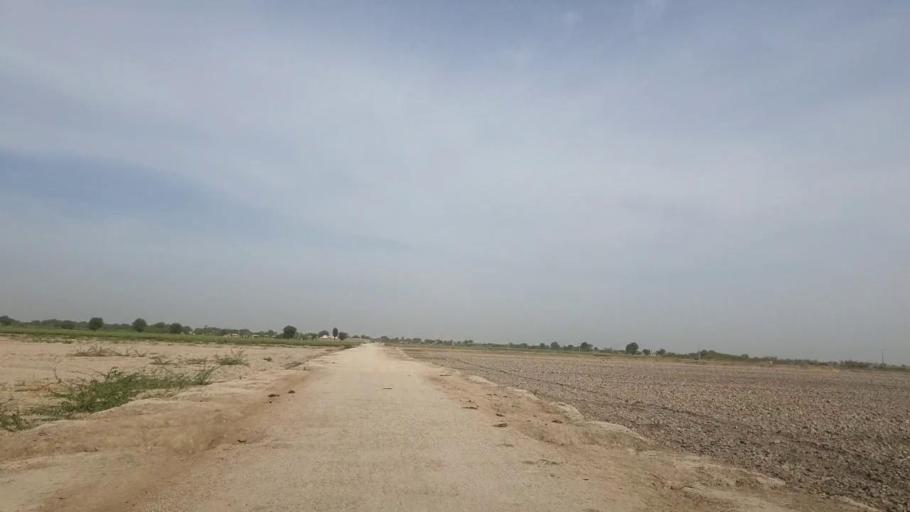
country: PK
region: Sindh
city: Kunri
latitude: 25.1724
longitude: 69.6175
